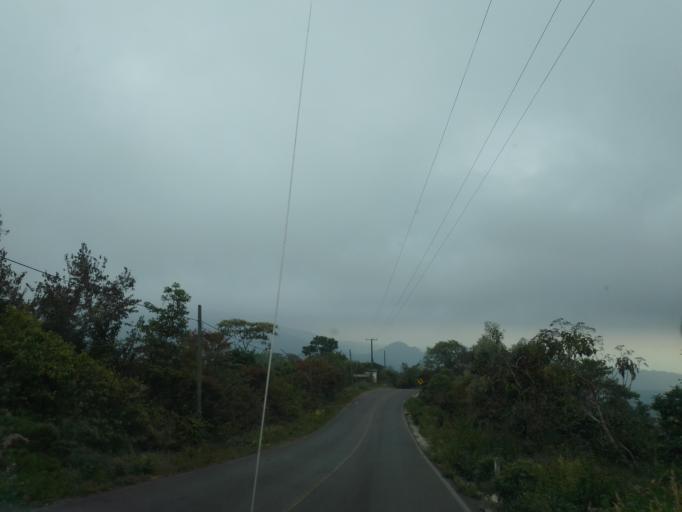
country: MX
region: Chiapas
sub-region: Union Juarez
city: Santo Domingo
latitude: 15.0810
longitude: -92.0822
